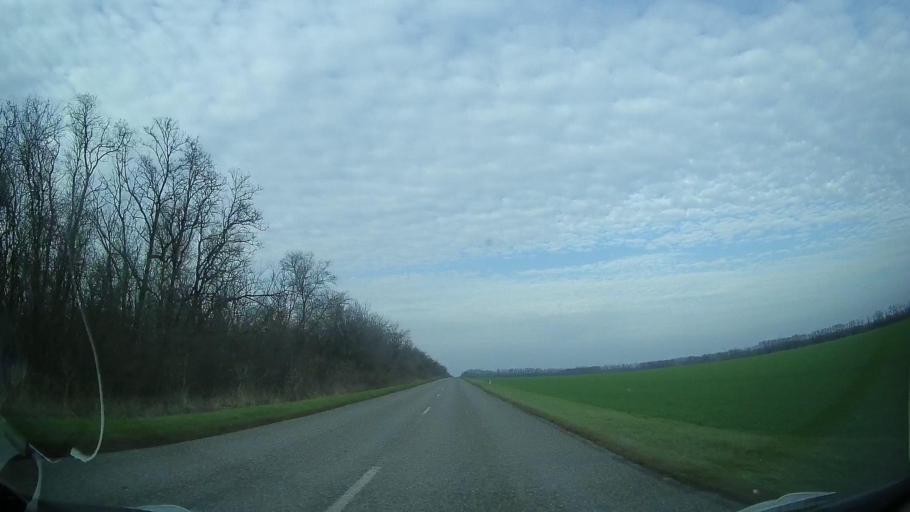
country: RU
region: Rostov
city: Zernograd
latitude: 46.9772
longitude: 40.3916
